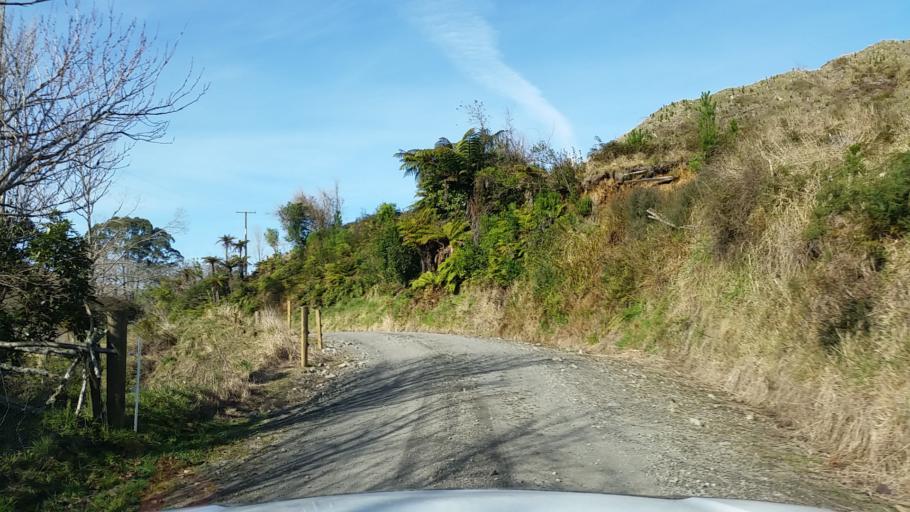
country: NZ
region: Taranaki
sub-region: South Taranaki District
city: Eltham
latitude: -39.3604
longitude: 174.5132
